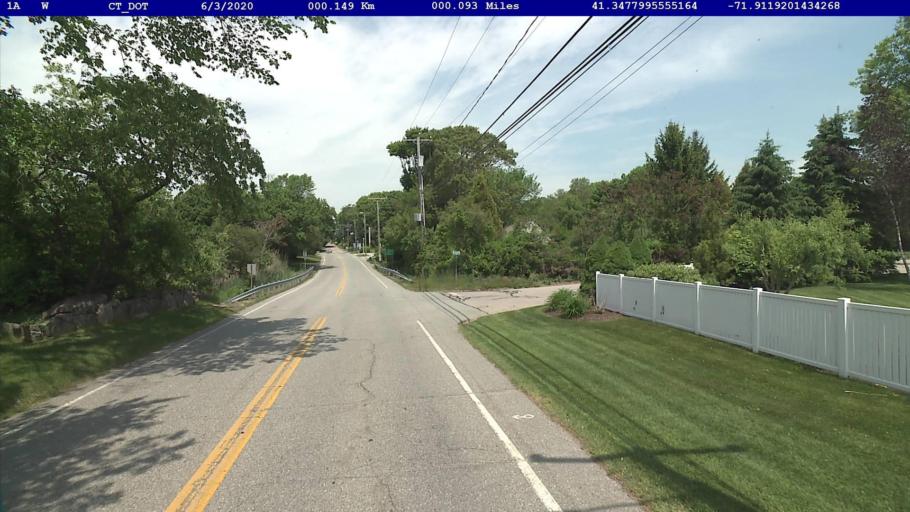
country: US
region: Connecticut
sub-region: New London County
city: Mystic
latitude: 41.3478
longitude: -71.9119
